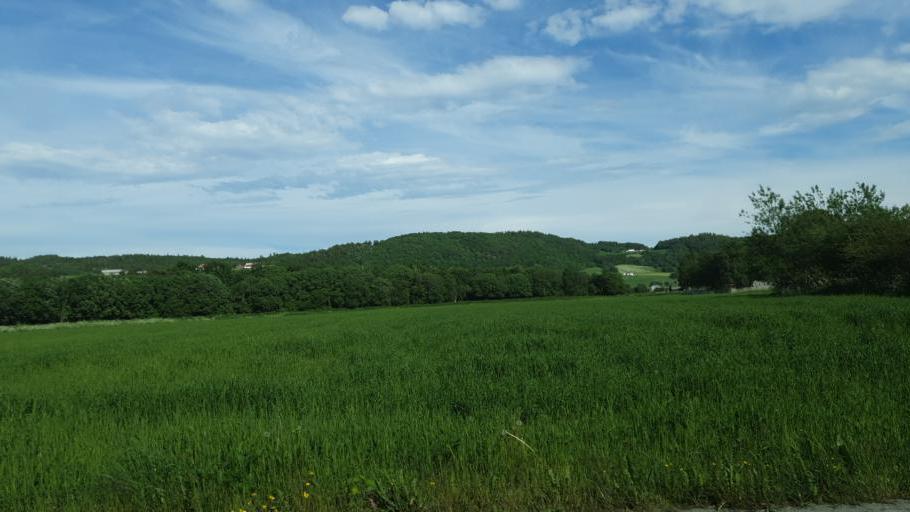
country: NO
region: Sor-Trondelag
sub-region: Rissa
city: Rissa
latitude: 63.5034
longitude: 10.0092
